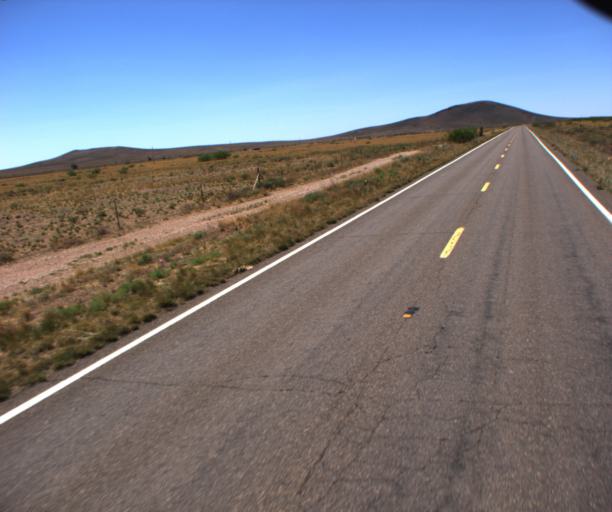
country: US
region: Arizona
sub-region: Cochise County
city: Douglas
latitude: 31.6458
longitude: -109.1689
